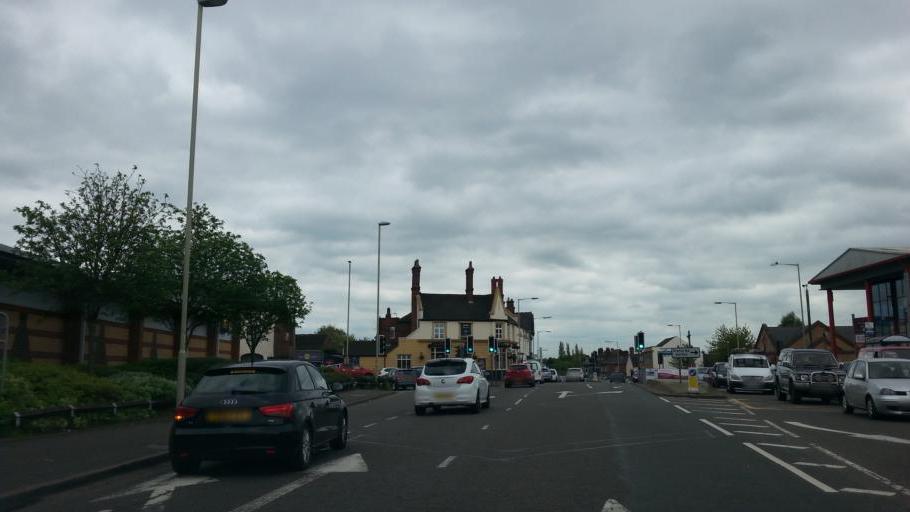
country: GB
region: England
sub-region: Dudley
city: Stourbridge
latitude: 52.4712
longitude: -2.1550
